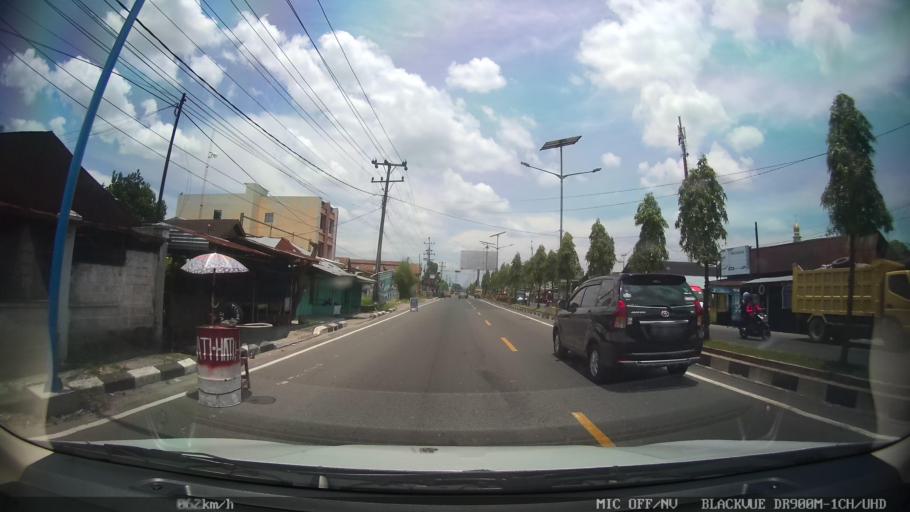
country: ID
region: North Sumatra
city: Binjai
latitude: 3.6078
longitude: 98.5189
